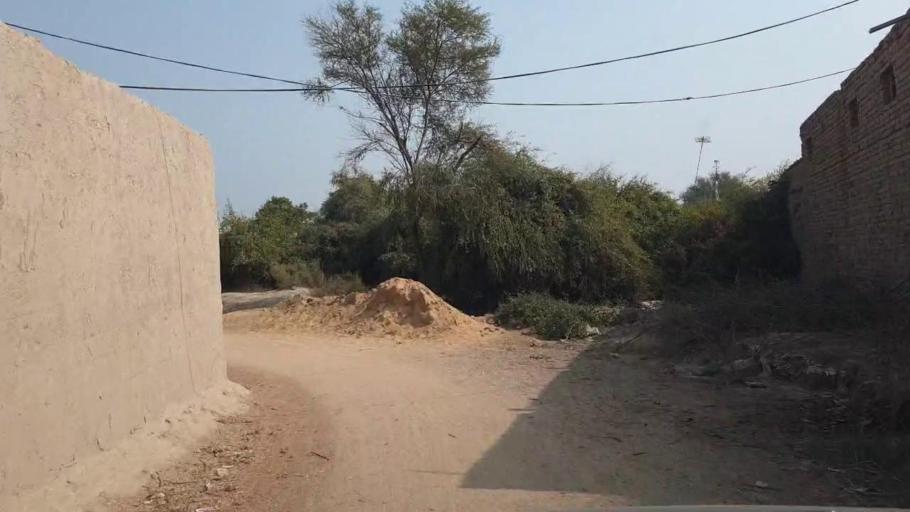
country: PK
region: Sindh
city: Bhit Shah
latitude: 25.8446
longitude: 68.4959
